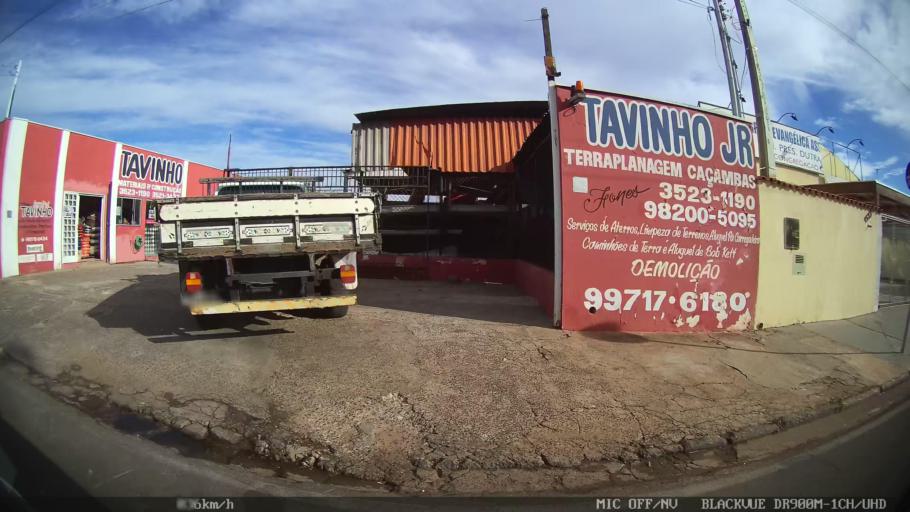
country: BR
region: Sao Paulo
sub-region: Catanduva
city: Catanduva
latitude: -21.1184
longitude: -48.9652
